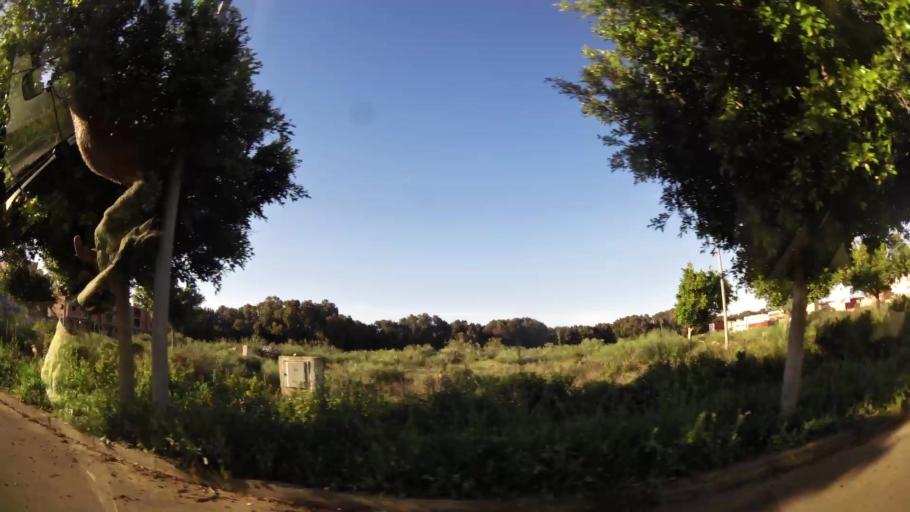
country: MA
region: Oriental
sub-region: Berkane-Taourirt
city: Madagh
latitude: 35.0875
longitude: -2.2510
